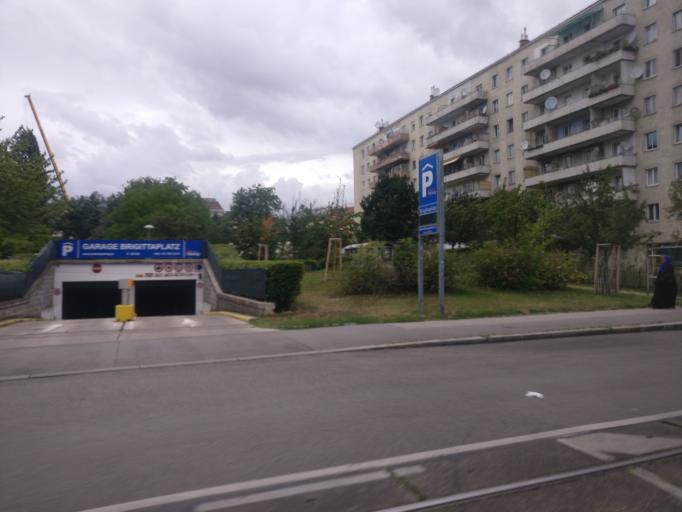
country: AT
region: Vienna
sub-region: Wien Stadt
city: Vienna
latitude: 48.2320
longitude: 16.3705
